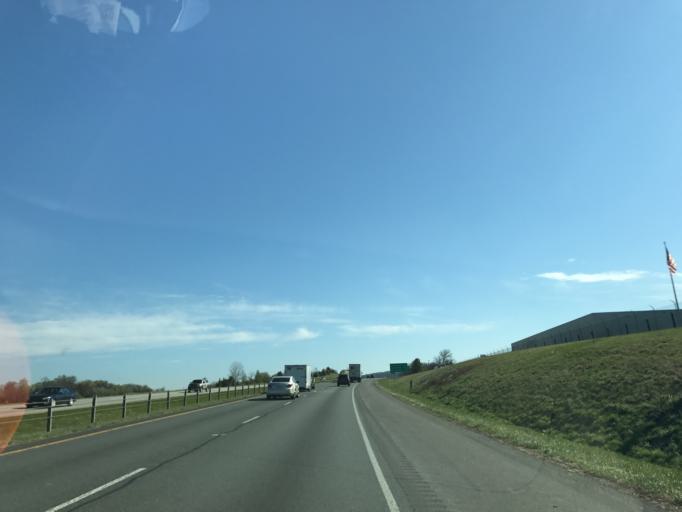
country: US
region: Virginia
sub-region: Rockingham County
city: Dayton
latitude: 38.4065
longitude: -78.9022
